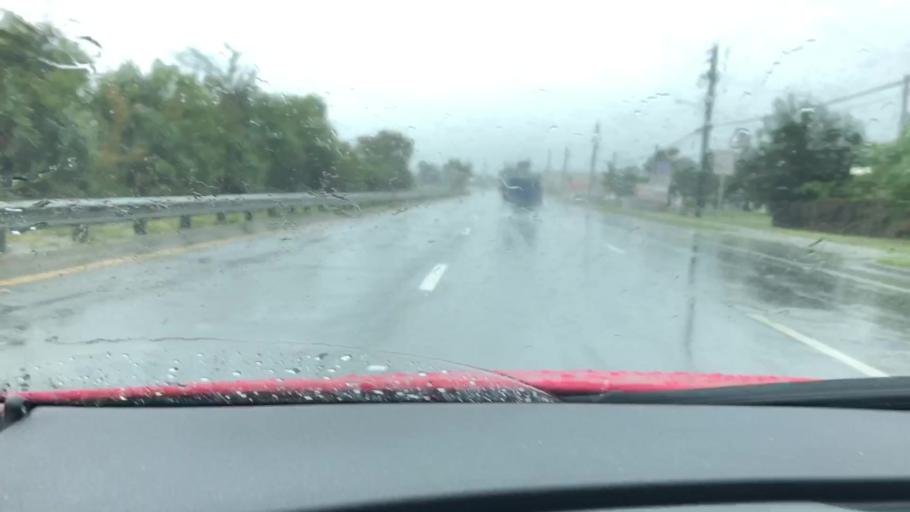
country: US
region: Florida
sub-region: Volusia County
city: South Daytona
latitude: 29.1709
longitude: -81.0259
